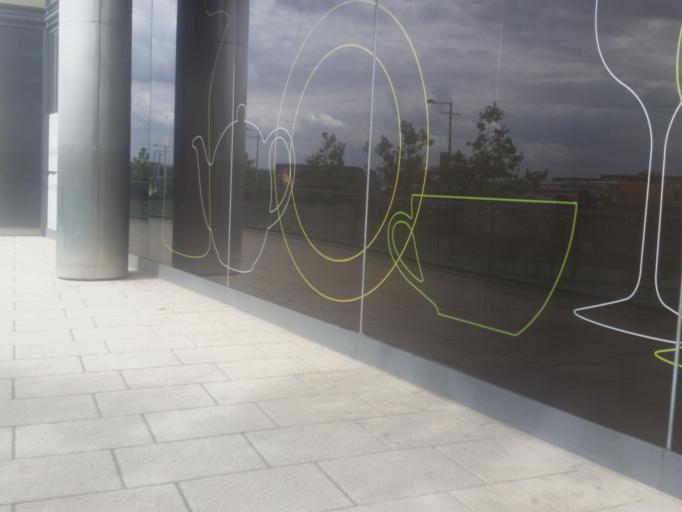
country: GB
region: England
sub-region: Greater London
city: Poplar
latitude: 51.5433
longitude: -0.0101
